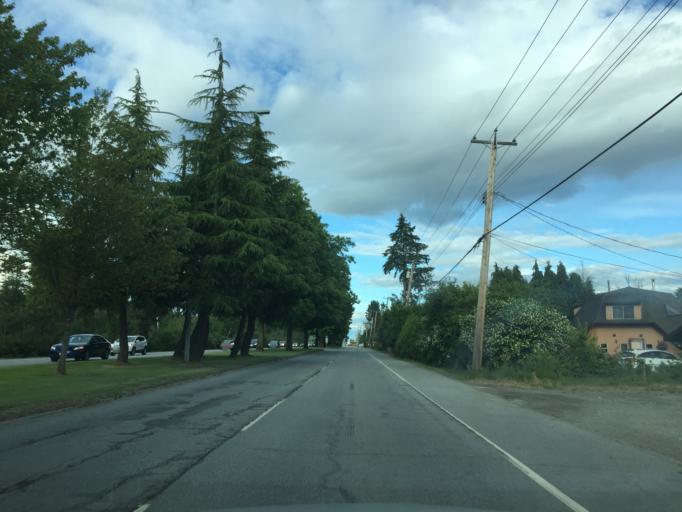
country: CA
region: British Columbia
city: Richmond
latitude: 49.1700
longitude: -123.0992
